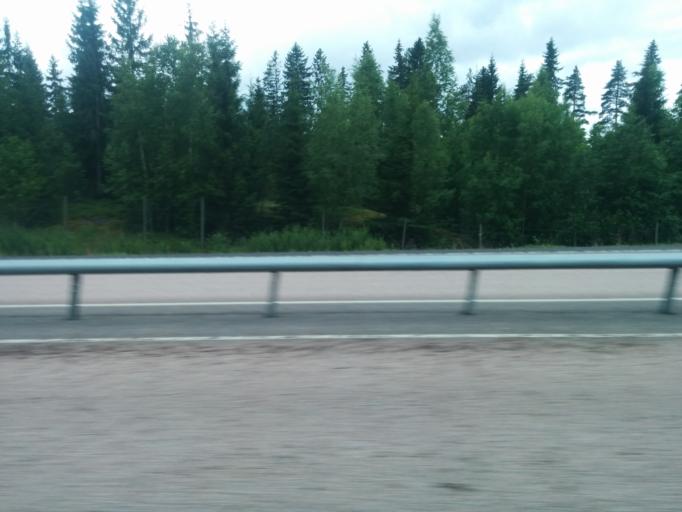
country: FI
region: Pirkanmaa
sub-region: Tampere
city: Orivesi
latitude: 61.7102
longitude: 24.5303
